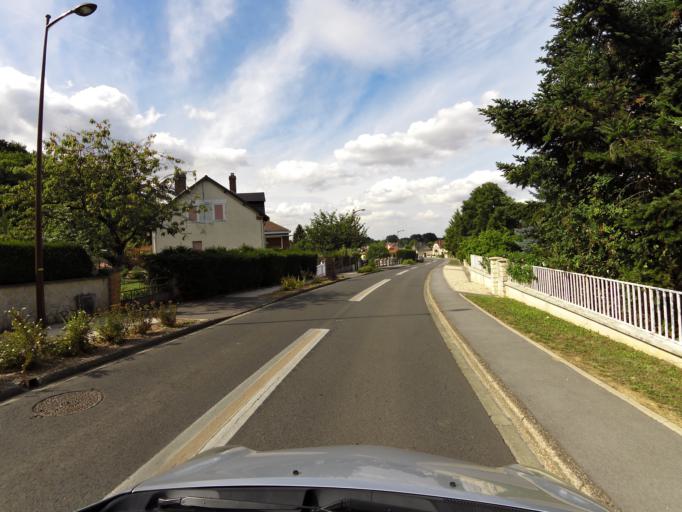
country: FR
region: Picardie
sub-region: Departement de l'Aisne
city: Bruyeres-et-Montberault
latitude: 49.5192
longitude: 3.6664
